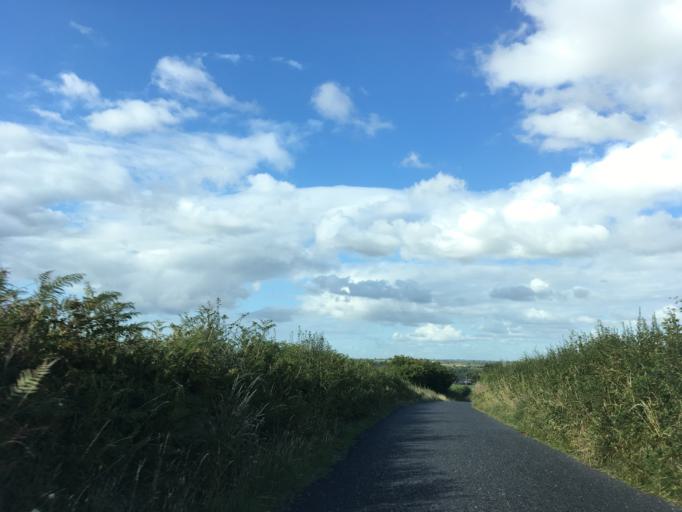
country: IE
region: Munster
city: Cahir
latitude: 52.2676
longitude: -7.9581
